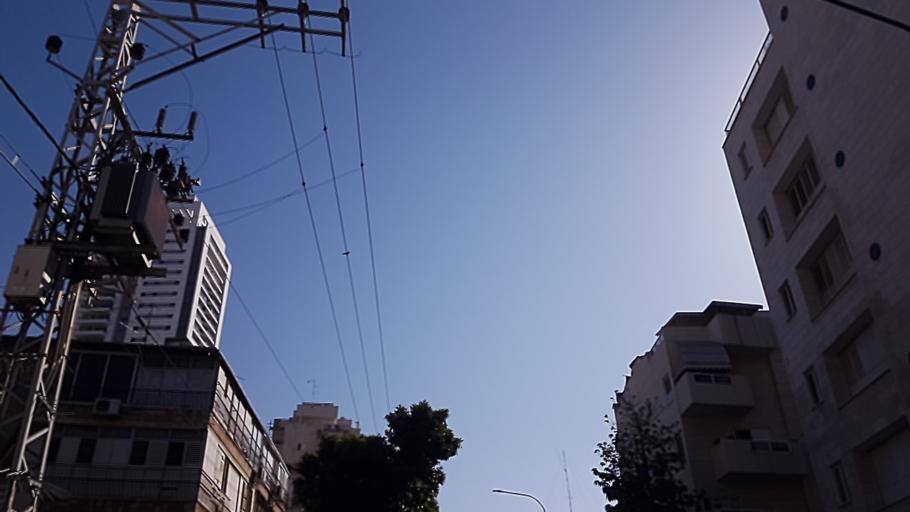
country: IL
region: Tel Aviv
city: Giv`atayim
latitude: 32.0716
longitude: 34.8229
